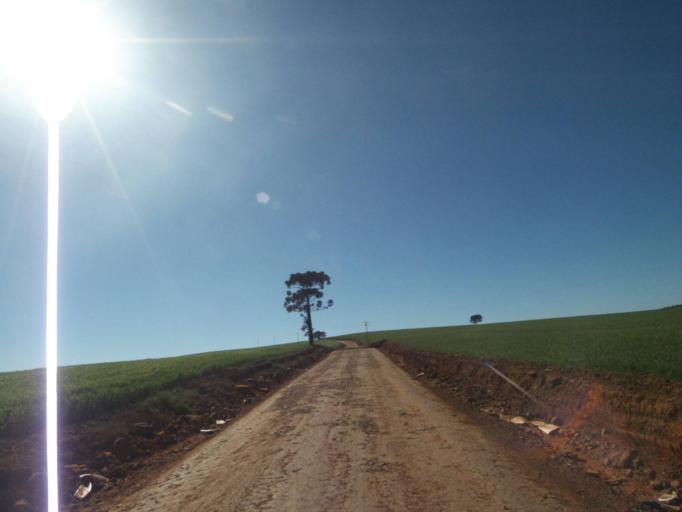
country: BR
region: Parana
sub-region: Tibagi
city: Tibagi
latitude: -24.6076
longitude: -50.6053
